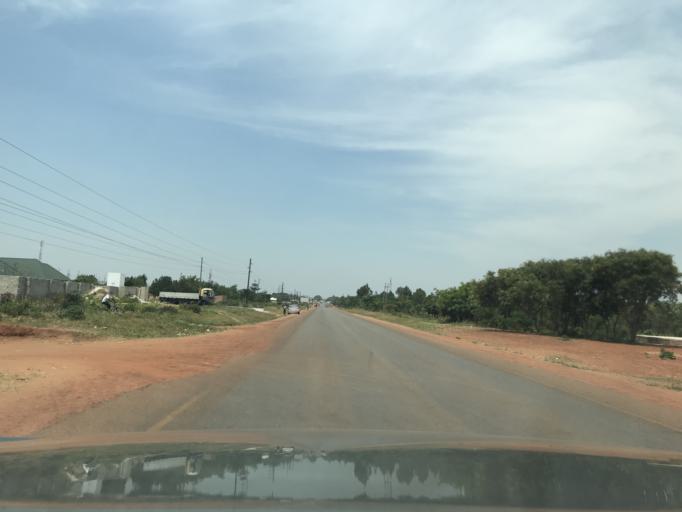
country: ZM
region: Northern
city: Kasama
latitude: -10.2124
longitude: 31.1591
